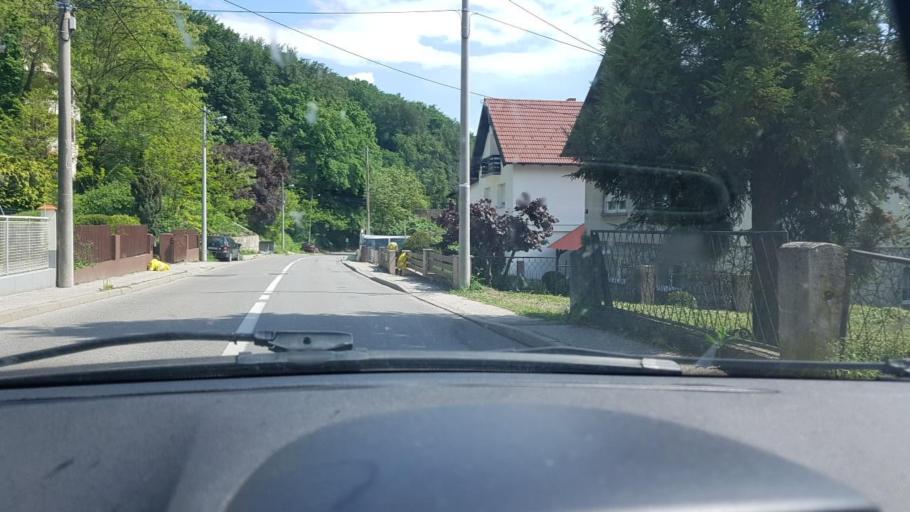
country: HR
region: Grad Zagreb
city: Dubrava
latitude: 45.8651
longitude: 16.0194
